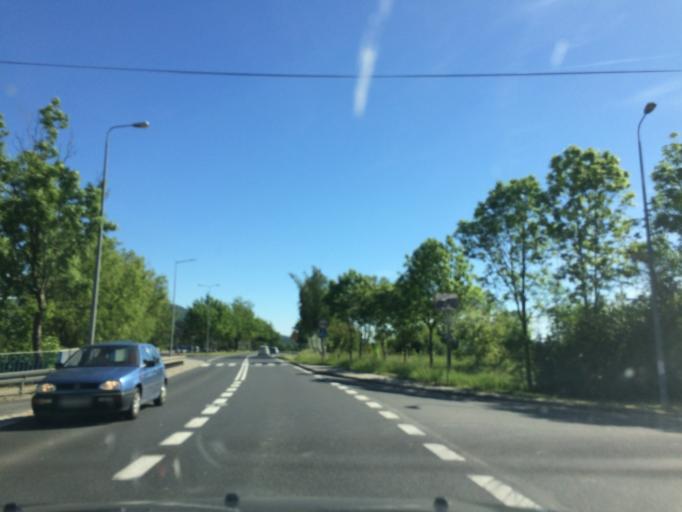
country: PL
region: Lower Silesian Voivodeship
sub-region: Powiat wroclawski
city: Sobotka
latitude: 50.9248
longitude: 16.6825
